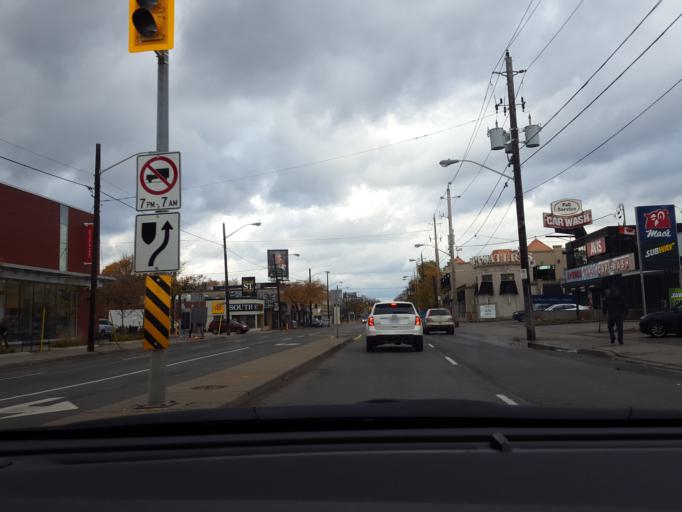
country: CA
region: Ontario
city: Toronto
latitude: 43.7222
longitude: -79.4155
